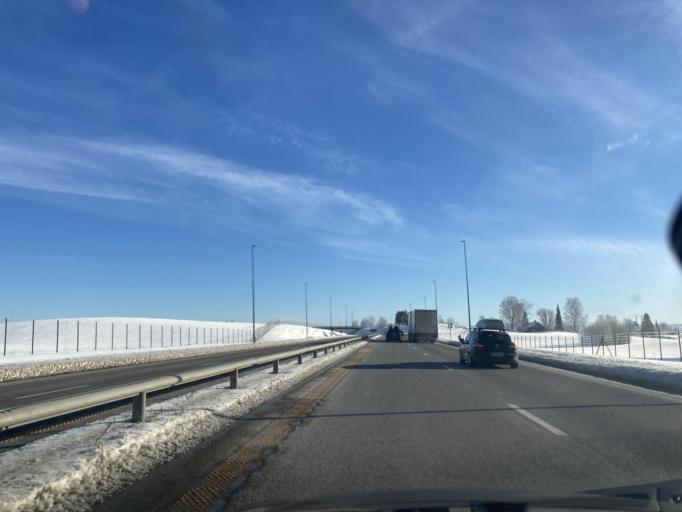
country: NO
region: Hedmark
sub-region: Loten
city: Loten
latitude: 60.8382
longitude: 11.3244
